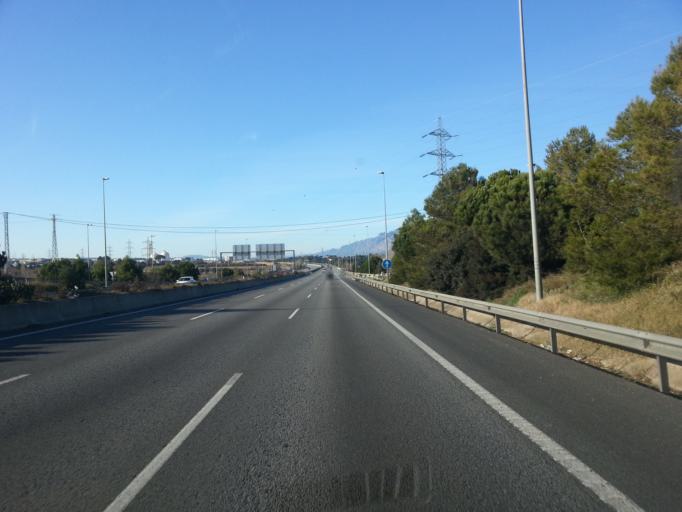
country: ES
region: Catalonia
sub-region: Provincia de Barcelona
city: Martorell
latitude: 41.4920
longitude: 1.9263
